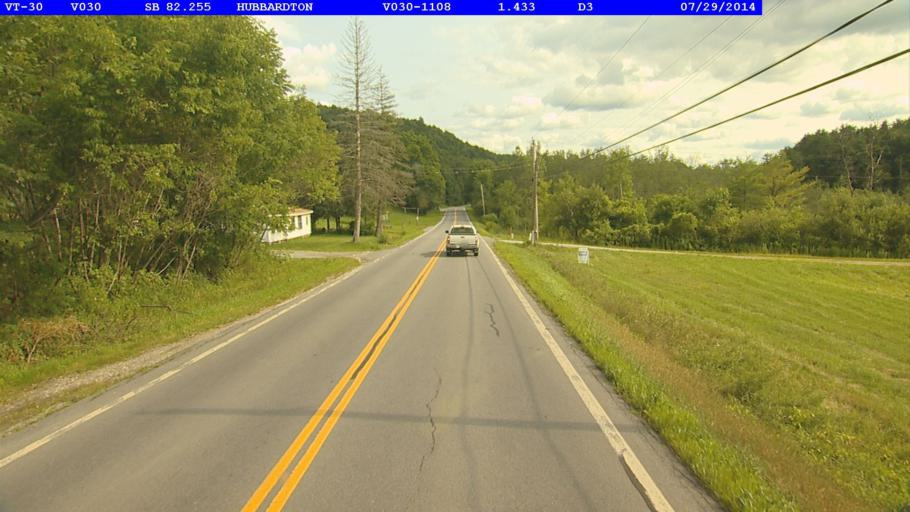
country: US
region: Vermont
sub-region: Rutland County
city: Castleton
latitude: 43.6986
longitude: -73.1851
